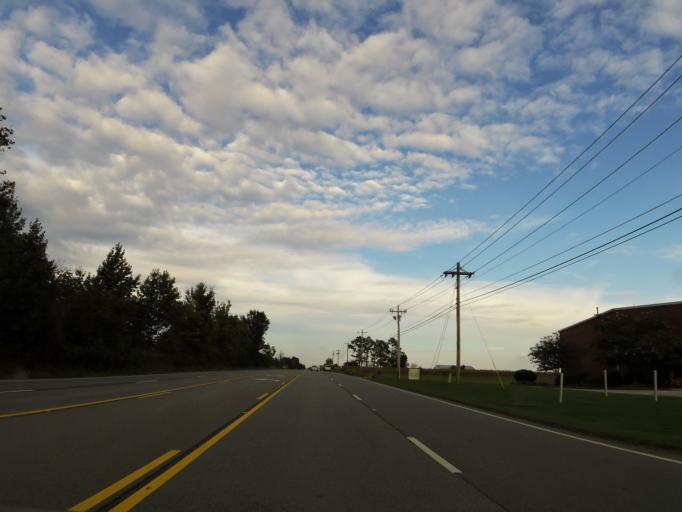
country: US
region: Alabama
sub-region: Lauderdale County
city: Rogersville
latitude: 34.8012
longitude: -87.1663
